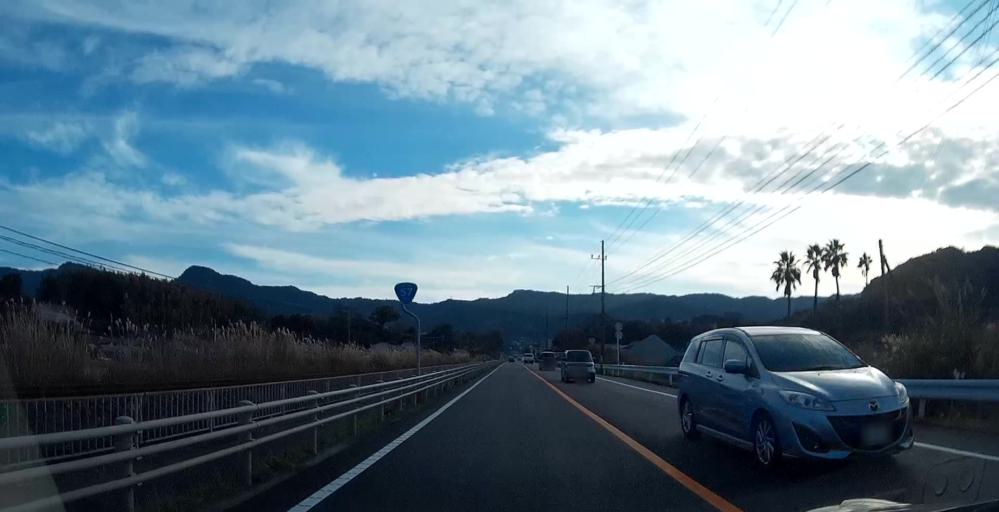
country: JP
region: Kumamoto
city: Uto
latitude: 32.6769
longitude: 130.5533
